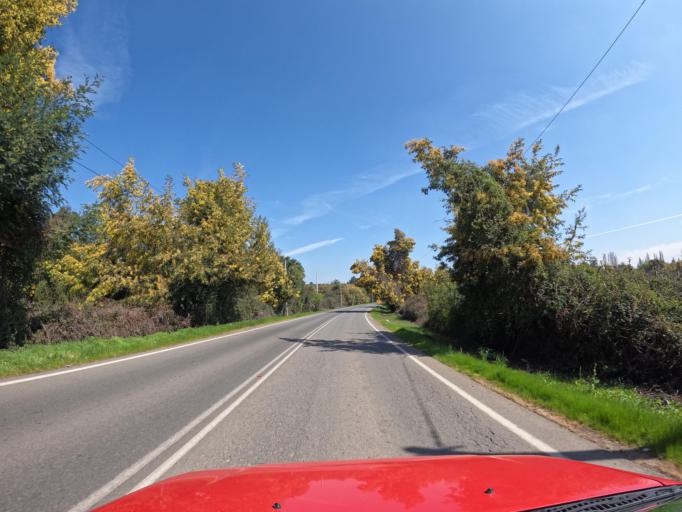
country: CL
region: Maule
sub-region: Provincia de Talca
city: San Clemente
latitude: -35.4886
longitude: -71.2948
